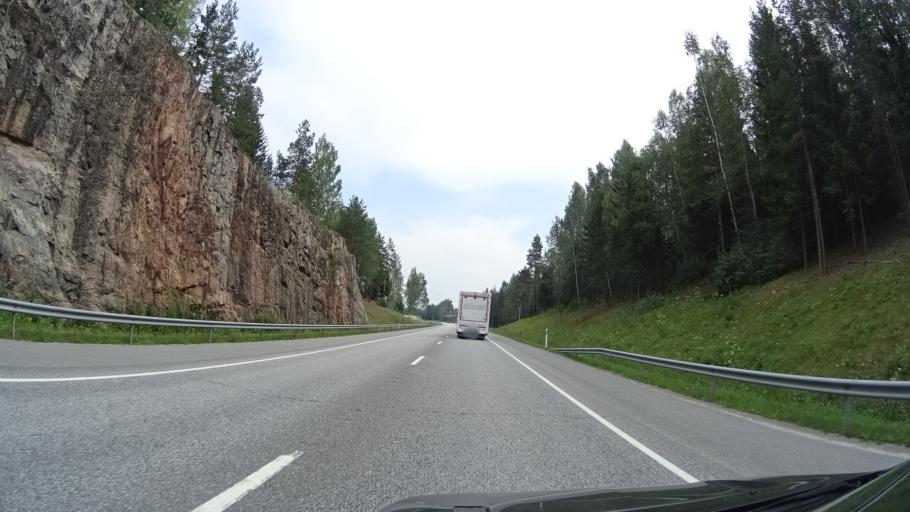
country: FI
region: Uusimaa
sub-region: Raaseporin
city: Karis
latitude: 60.0713
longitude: 23.7780
